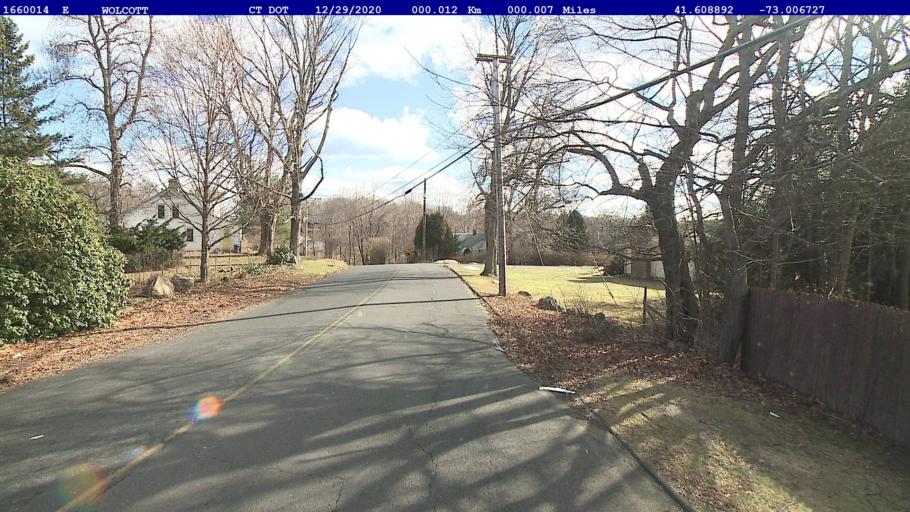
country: US
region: Connecticut
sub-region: New Haven County
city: Wolcott
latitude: 41.6089
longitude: -73.0067
